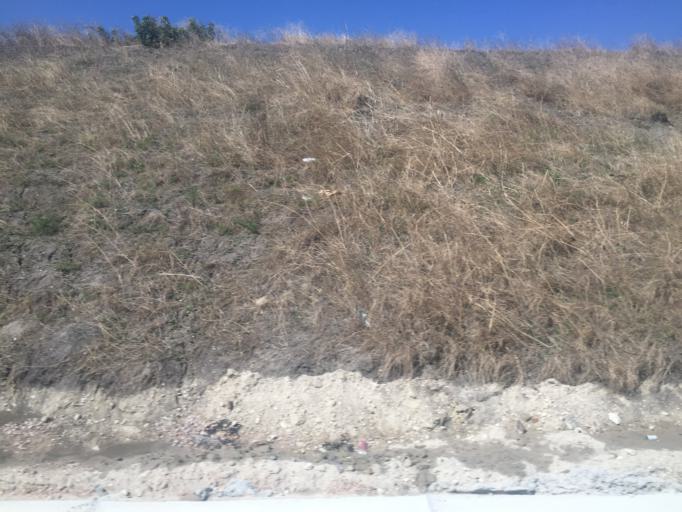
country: TR
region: Balikesir
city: Susurluk
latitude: 39.9630
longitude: 28.1645
